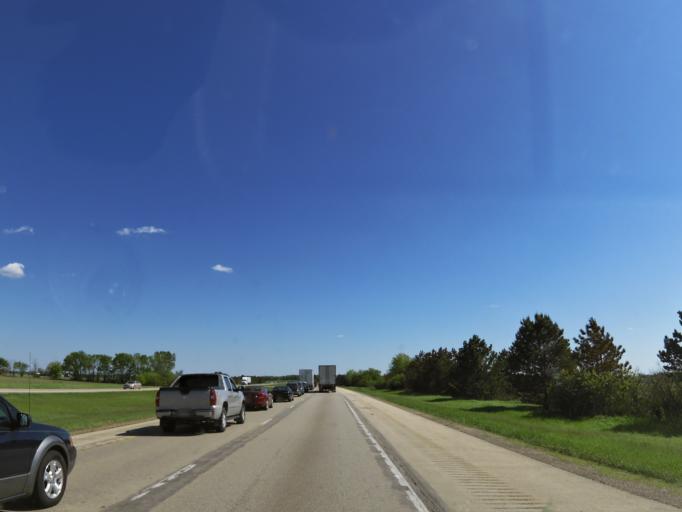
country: US
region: Illinois
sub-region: Ogle County
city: Davis Junction
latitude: 42.0665
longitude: -89.0219
